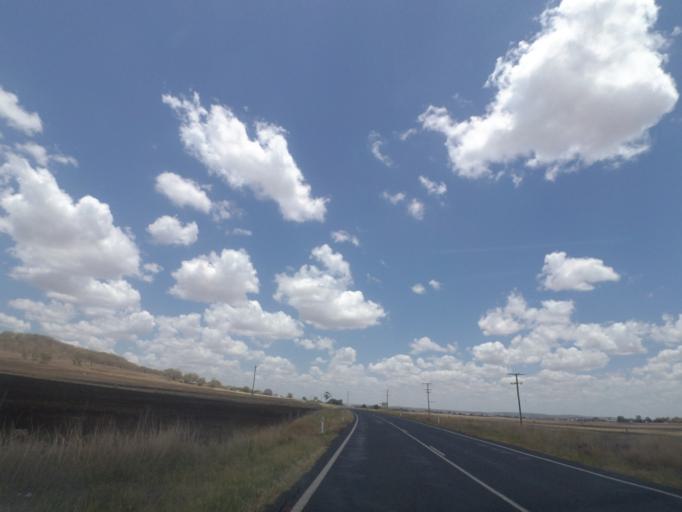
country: AU
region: Queensland
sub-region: Southern Downs
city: Warwick
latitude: -28.0139
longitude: 151.9871
